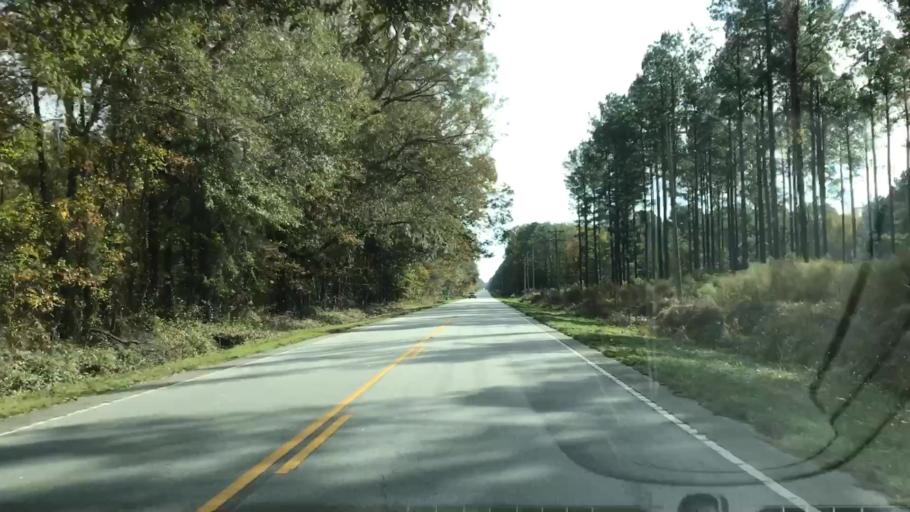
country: US
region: South Carolina
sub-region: Colleton County
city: Walterboro
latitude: 32.8217
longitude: -80.5533
